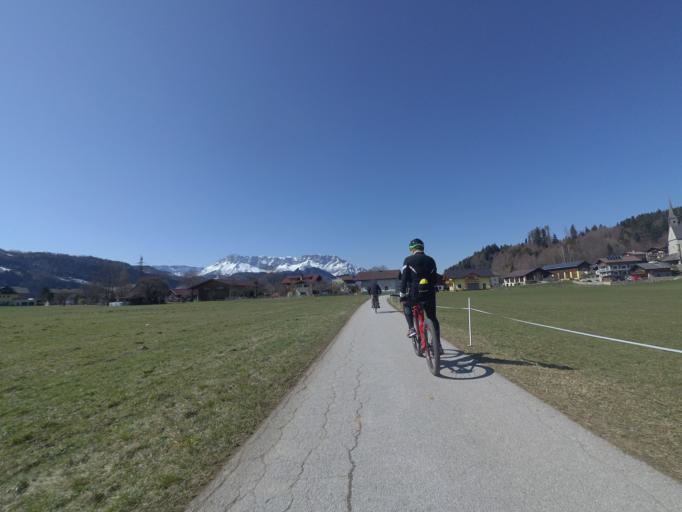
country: AT
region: Salzburg
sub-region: Politischer Bezirk Hallein
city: Adnet
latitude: 47.6731
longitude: 13.1304
